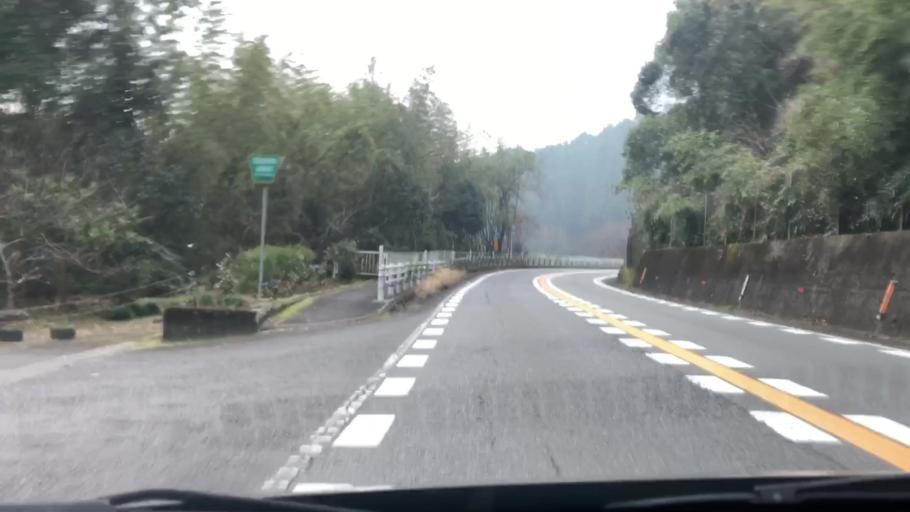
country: JP
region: Oita
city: Usuki
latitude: 33.0242
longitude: 131.6942
